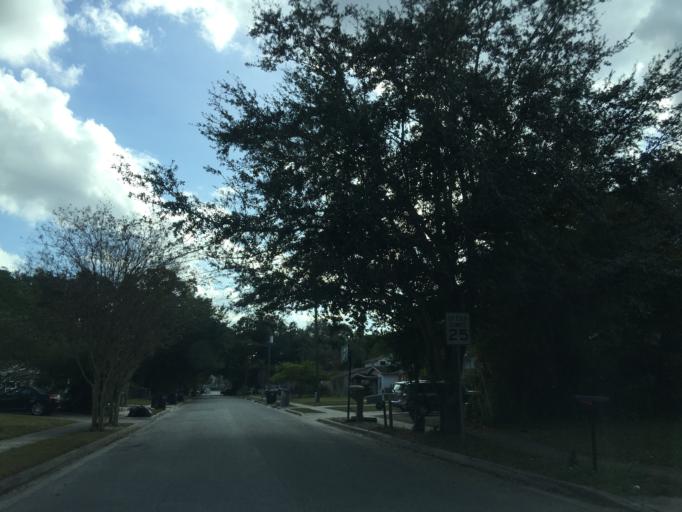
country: US
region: Florida
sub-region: Orange County
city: Eatonville
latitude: 28.6212
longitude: -81.3939
